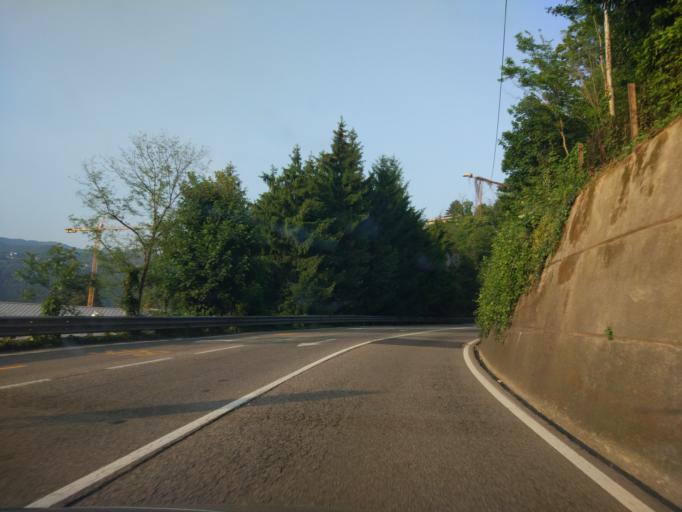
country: IT
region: Lombardy
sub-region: Provincia di Como
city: Como
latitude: 45.7902
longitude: 9.0951
